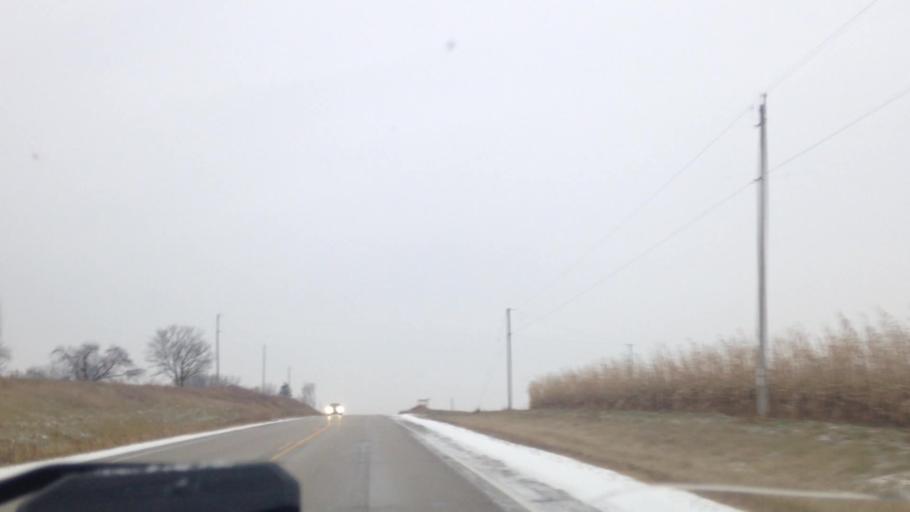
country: US
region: Wisconsin
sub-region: Dodge County
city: Hustisford
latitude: 43.3866
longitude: -88.5419
